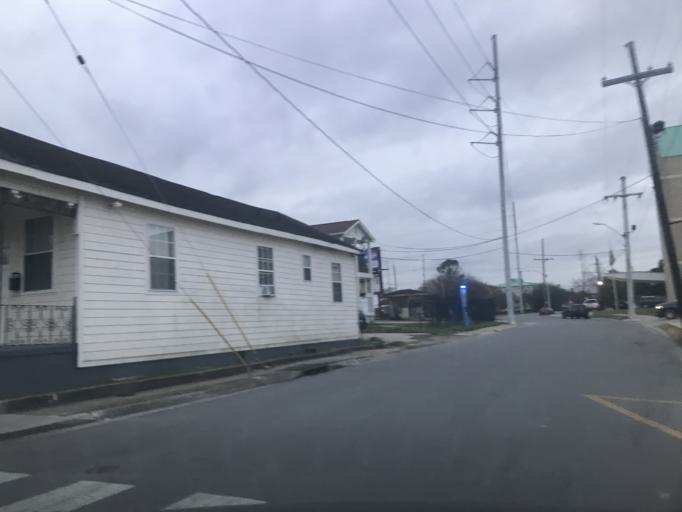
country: US
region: Louisiana
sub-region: Orleans Parish
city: New Orleans
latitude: 29.9624
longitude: -90.1050
